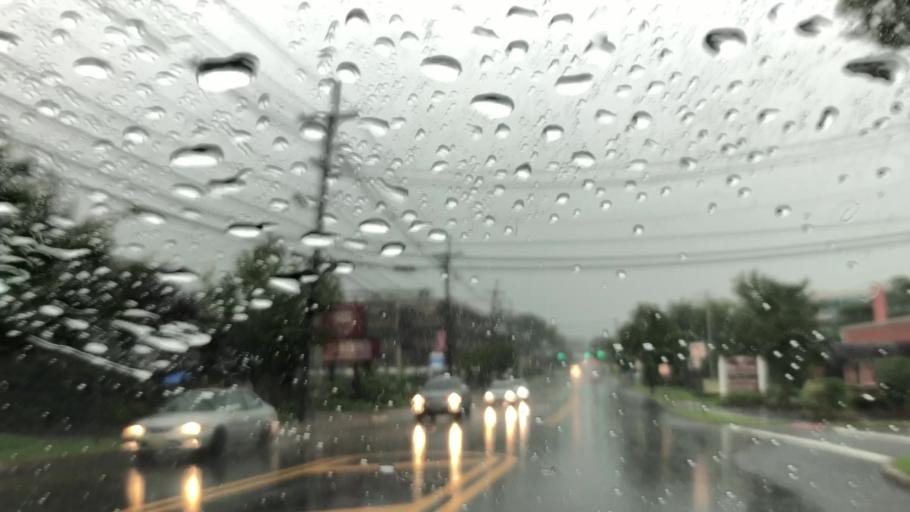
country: US
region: New Jersey
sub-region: Bergen County
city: Saddle Brook
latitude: 40.8967
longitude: -74.0942
